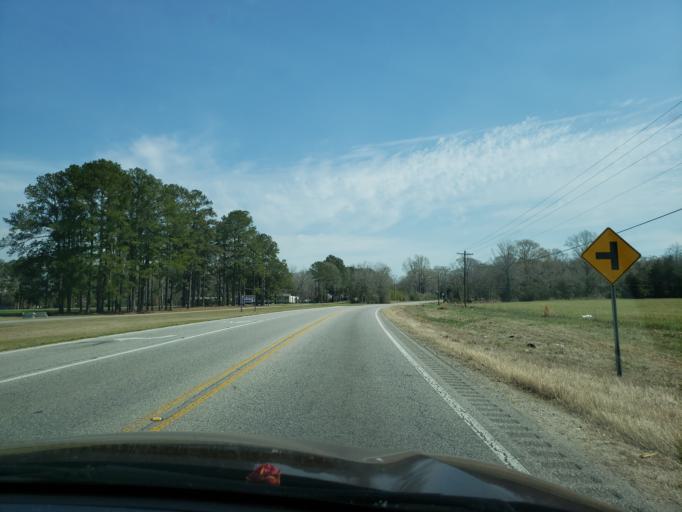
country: US
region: Alabama
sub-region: Elmore County
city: Elmore
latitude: 32.5497
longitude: -86.2871
